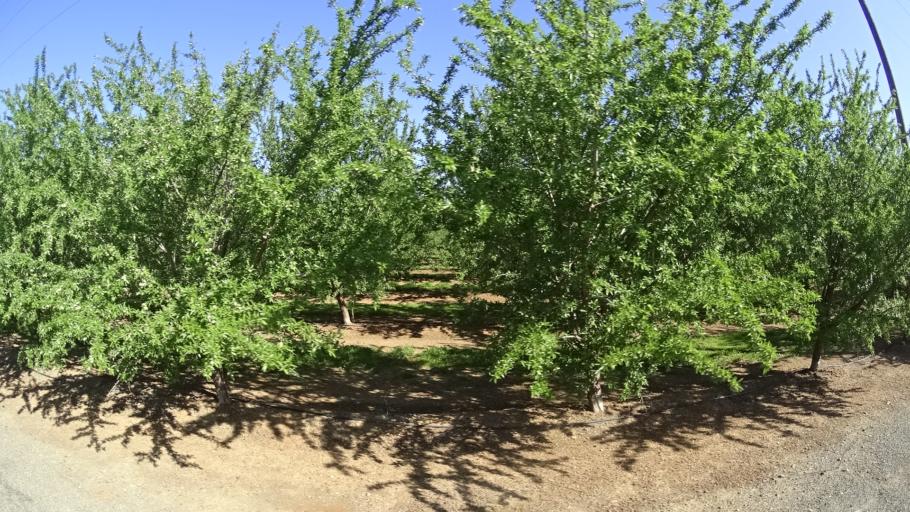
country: US
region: California
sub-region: Glenn County
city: Hamilton City
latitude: 39.7757
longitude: -122.1009
